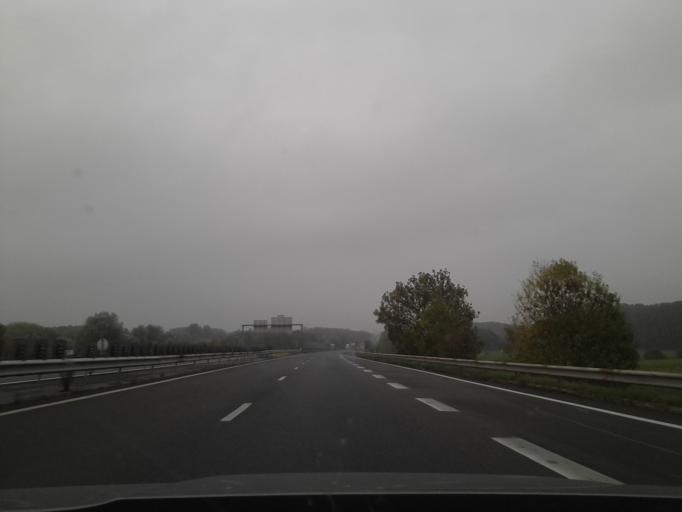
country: FR
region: Nord-Pas-de-Calais
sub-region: Departement du Nord
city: Hordain
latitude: 50.2510
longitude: 3.3178
